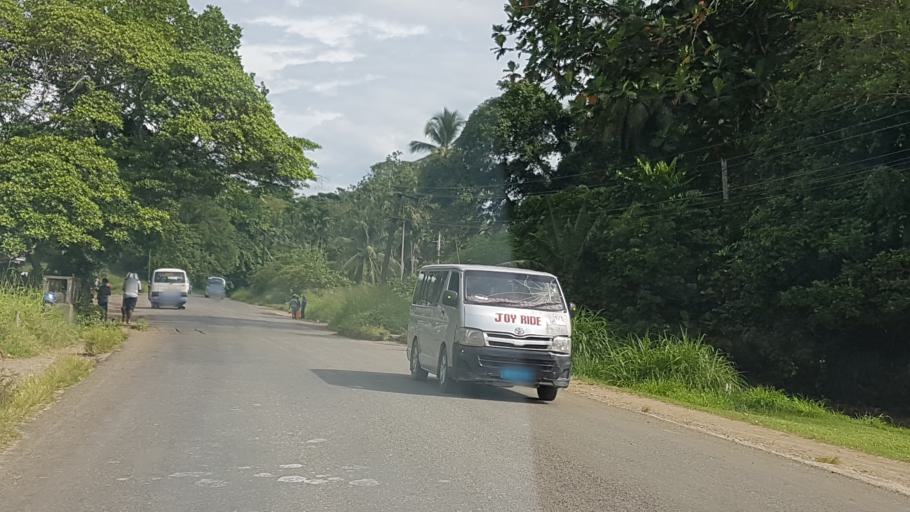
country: PG
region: Madang
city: Madang
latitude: -5.2000
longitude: 145.7742
